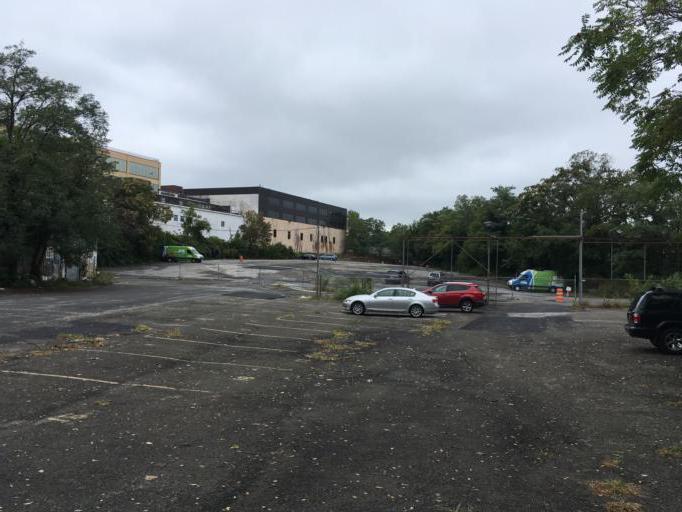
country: US
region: New York
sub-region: Kings County
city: Bensonhurst
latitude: 40.6345
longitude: -74.0112
